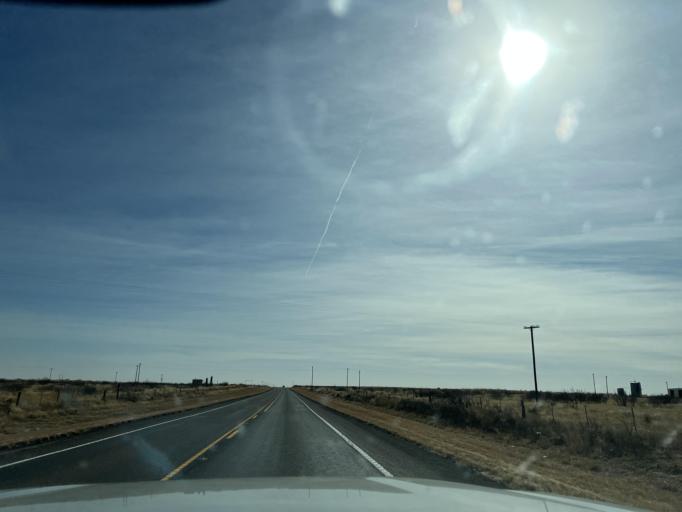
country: US
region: Texas
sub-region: Andrews County
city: Andrews
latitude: 32.4467
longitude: -102.4460
